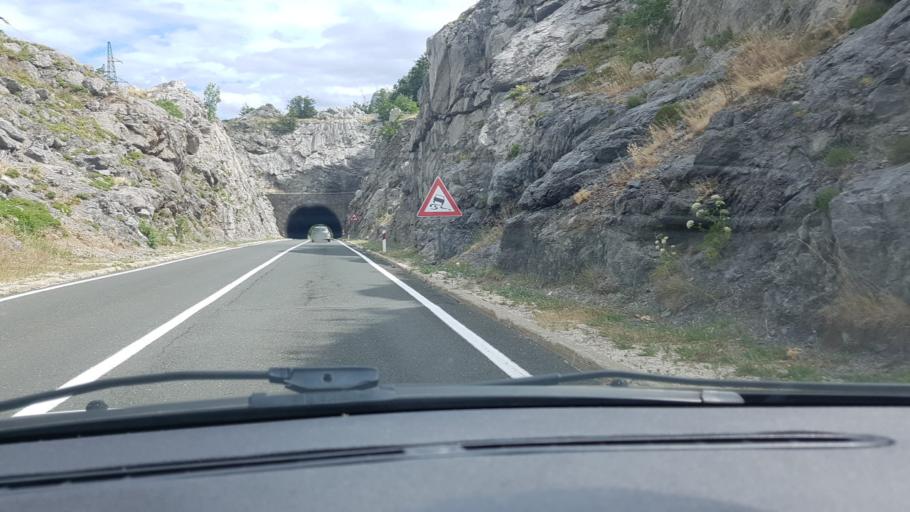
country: HR
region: Zadarska
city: Gracac
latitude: 44.2494
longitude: 15.8082
